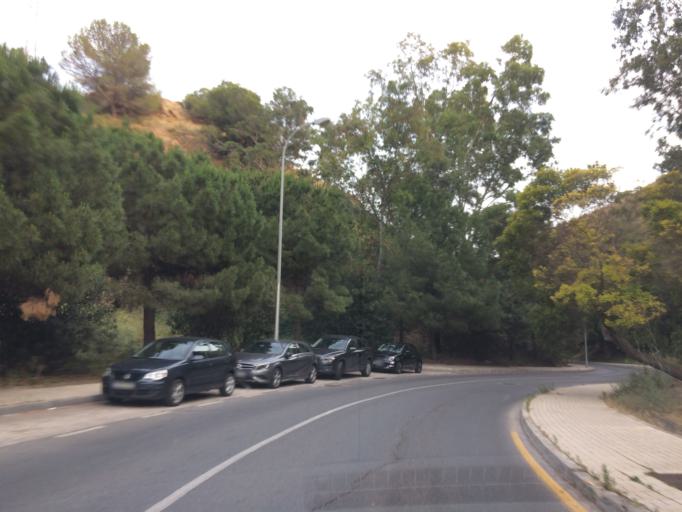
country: ES
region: Andalusia
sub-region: Provincia de Malaga
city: Malaga
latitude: 36.7341
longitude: -4.4048
